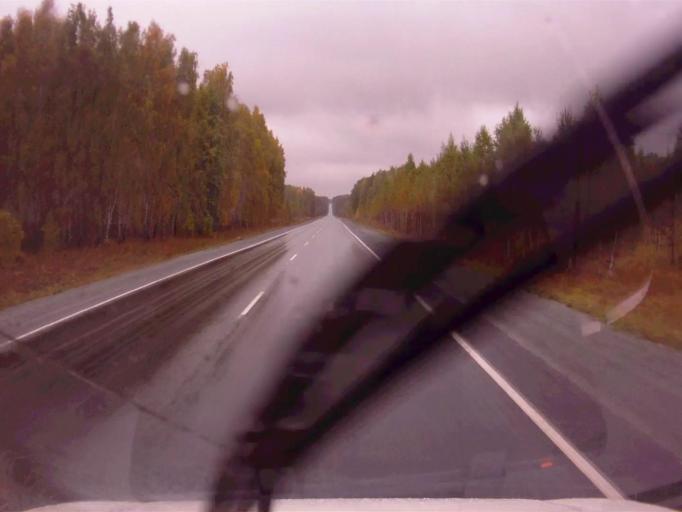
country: RU
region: Chelyabinsk
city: Tayginka
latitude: 55.5098
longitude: 60.6381
